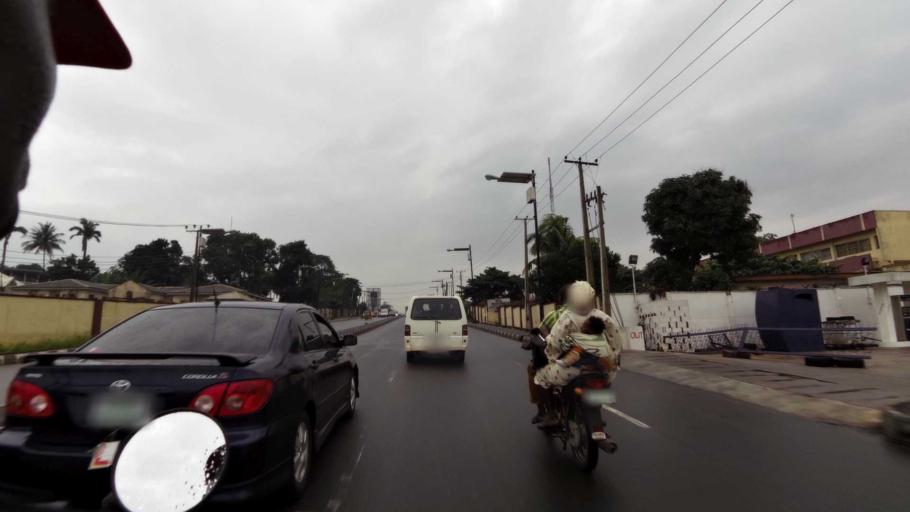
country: NG
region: Oyo
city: Ibadan
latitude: 7.3977
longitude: 3.9142
